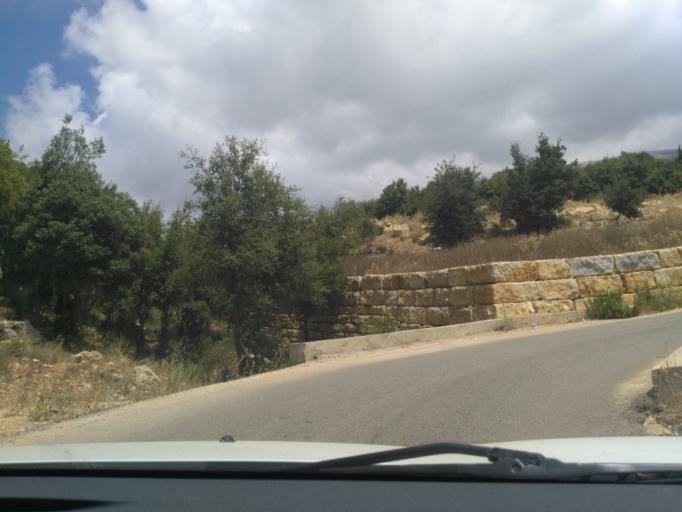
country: LB
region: Mont-Liban
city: Beit ed Dine
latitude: 33.6882
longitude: 35.6673
